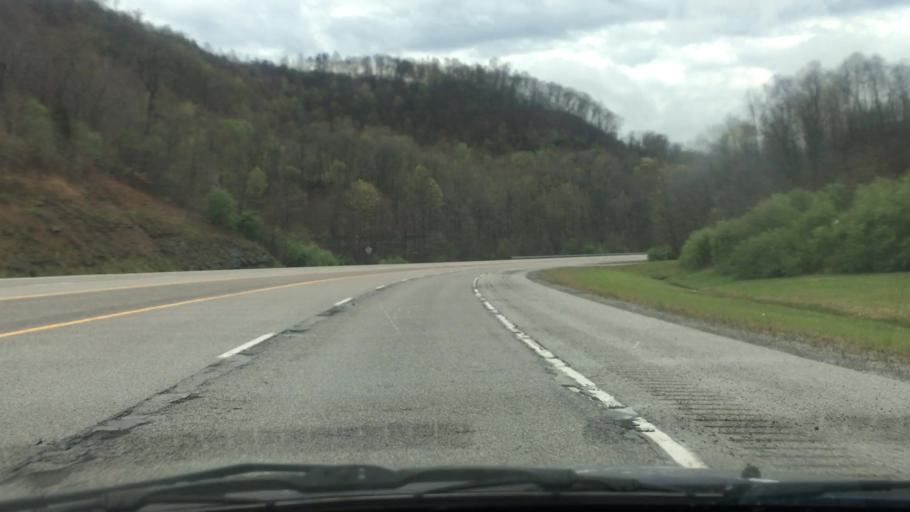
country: US
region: Kentucky
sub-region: Letcher County
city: Jenkins
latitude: 37.2124
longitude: -82.6242
